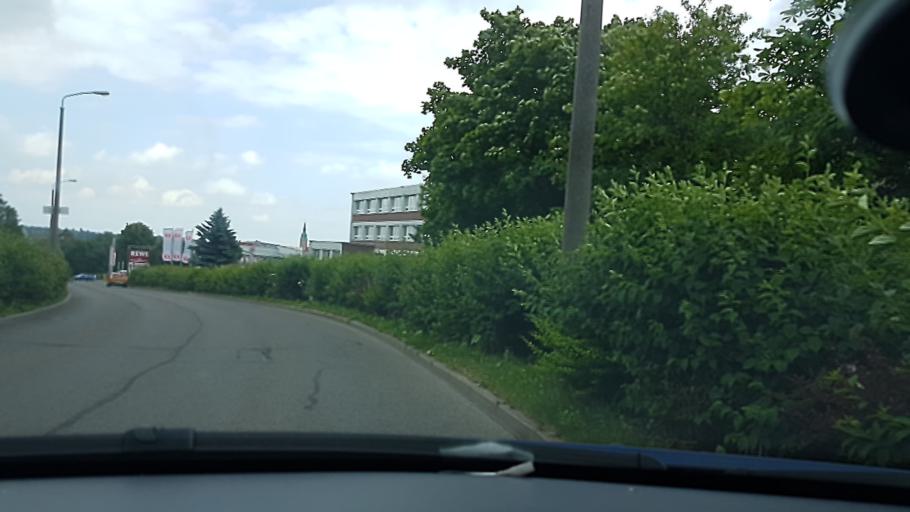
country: DE
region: Saxony
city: Freiberg
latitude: 50.9182
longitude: 13.3261
